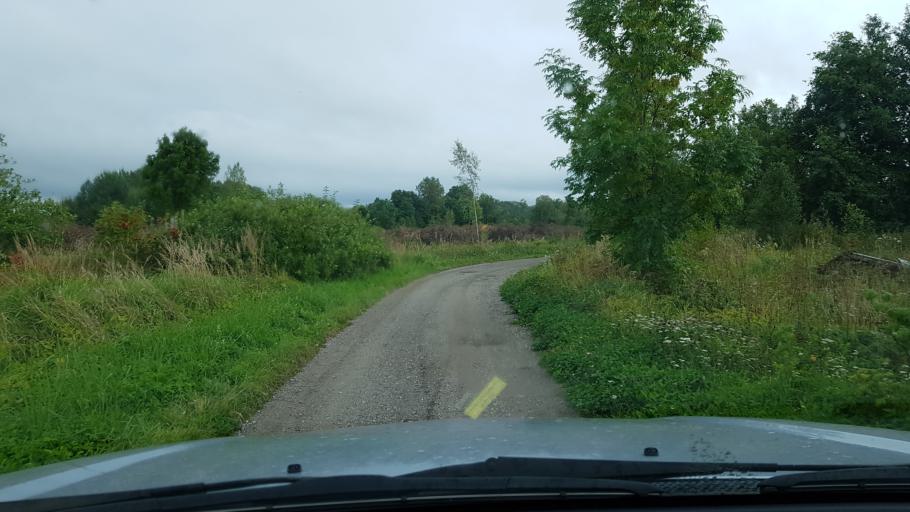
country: EE
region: Harju
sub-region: Joelaehtme vald
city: Loo
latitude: 59.4044
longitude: 24.9272
